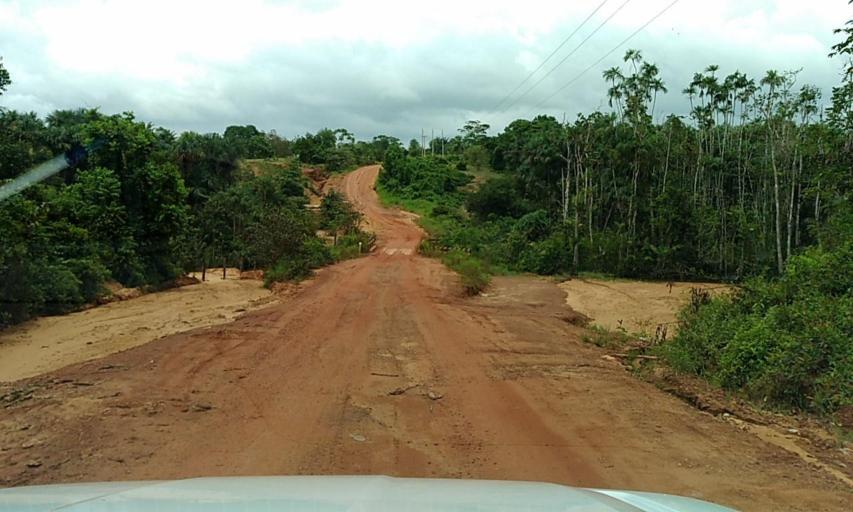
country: BR
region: Para
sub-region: Senador Jose Porfirio
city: Senador Jose Porfirio
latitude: -2.6161
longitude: -51.8700
